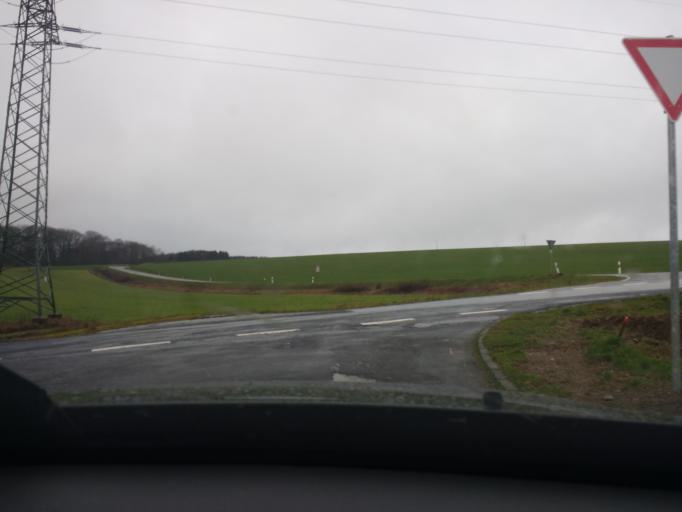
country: DE
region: Rheinland-Pfalz
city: Paschel
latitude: 49.6383
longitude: 6.6828
